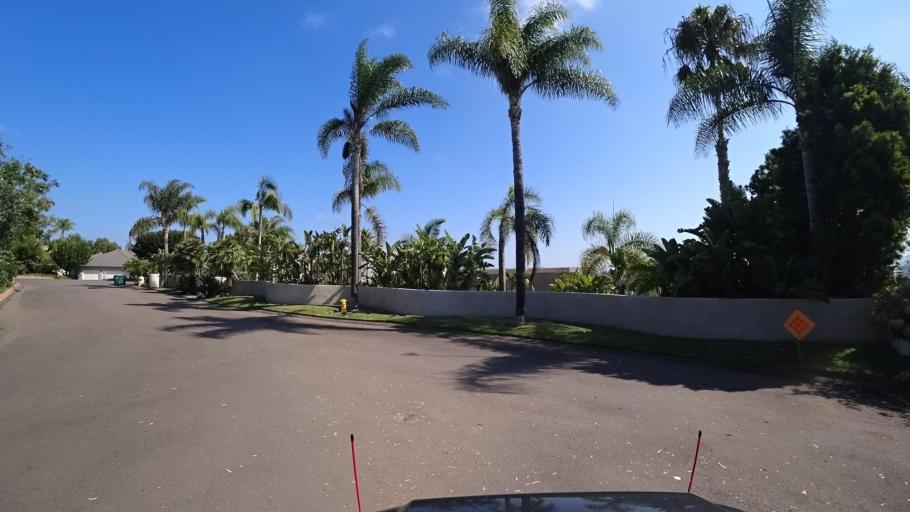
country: US
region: California
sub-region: San Diego County
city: Solana Beach
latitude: 32.9845
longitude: -117.2320
